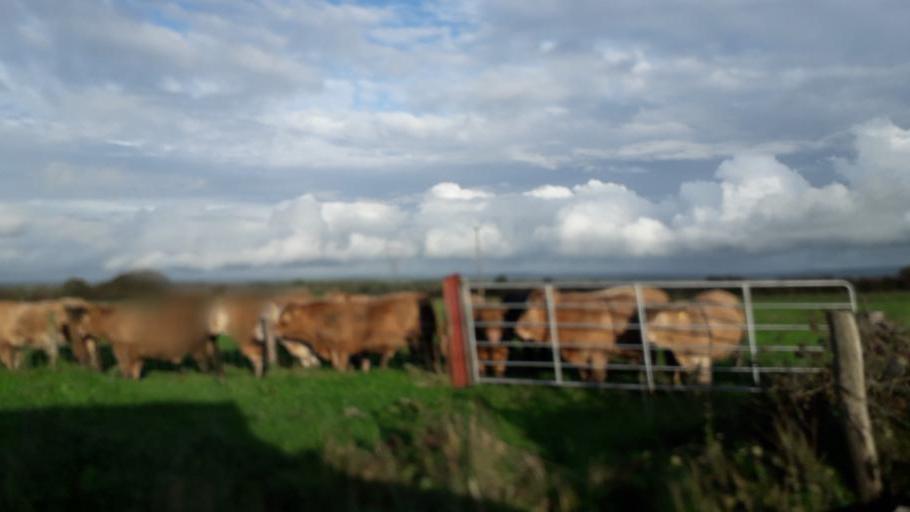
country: IE
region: Connaught
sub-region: Roscommon
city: Boyle
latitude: 53.7955
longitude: -8.2888
